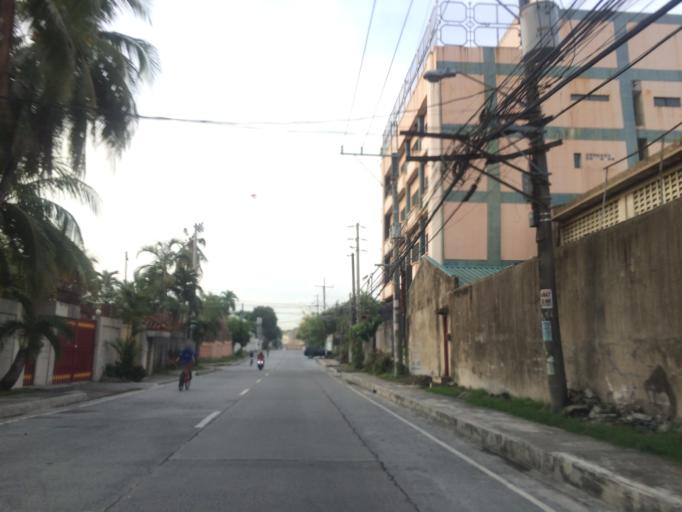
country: PH
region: Calabarzon
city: Del Monte
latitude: 14.6313
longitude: 121.0052
